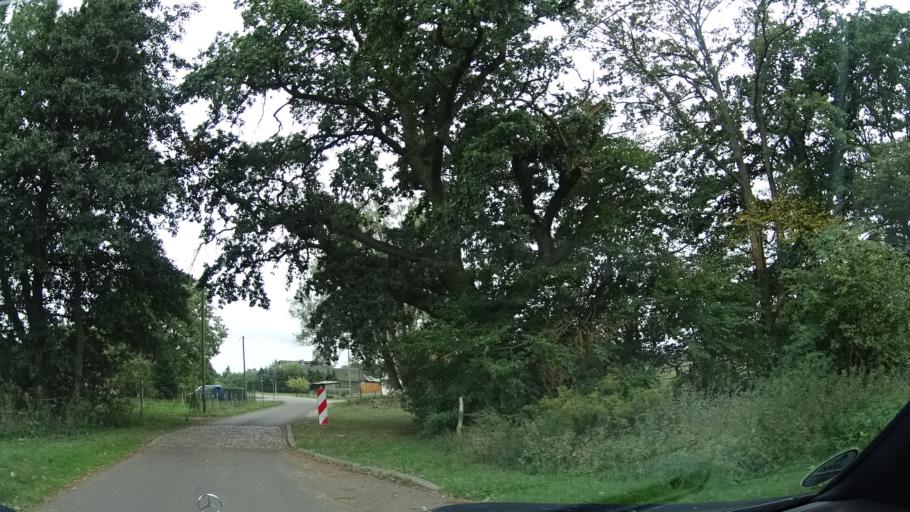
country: DE
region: Brandenburg
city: Neuruppin
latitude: 52.9612
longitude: 12.7618
